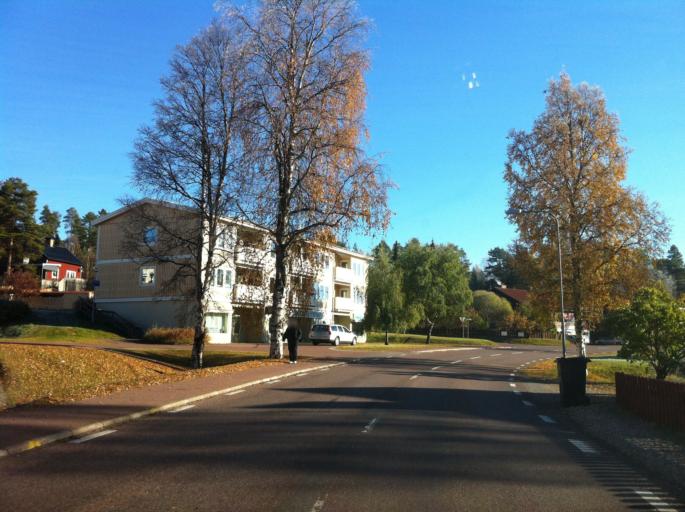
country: NO
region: Hedmark
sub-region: Trysil
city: Innbygda
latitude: 61.8580
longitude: 12.7243
